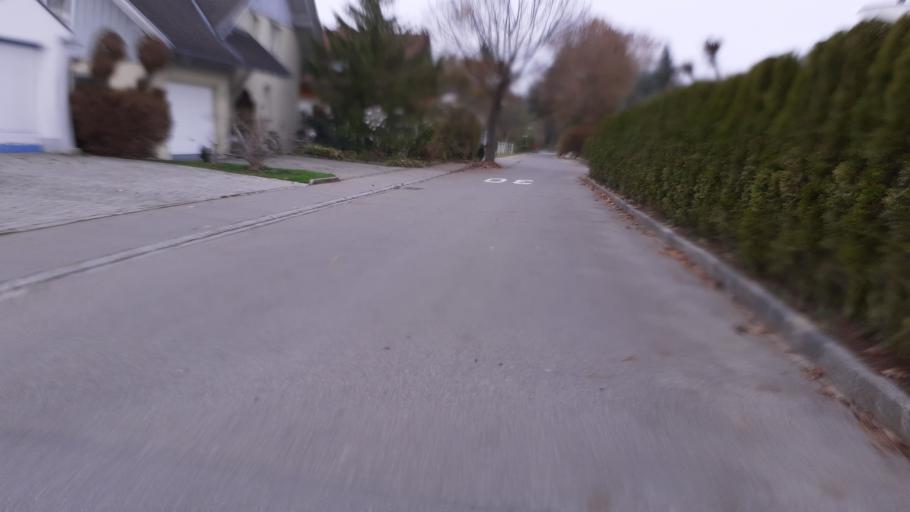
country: AT
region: Vorarlberg
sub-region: Politischer Bezirk Feldkirch
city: Nofels
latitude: 47.2627
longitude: 9.5901
